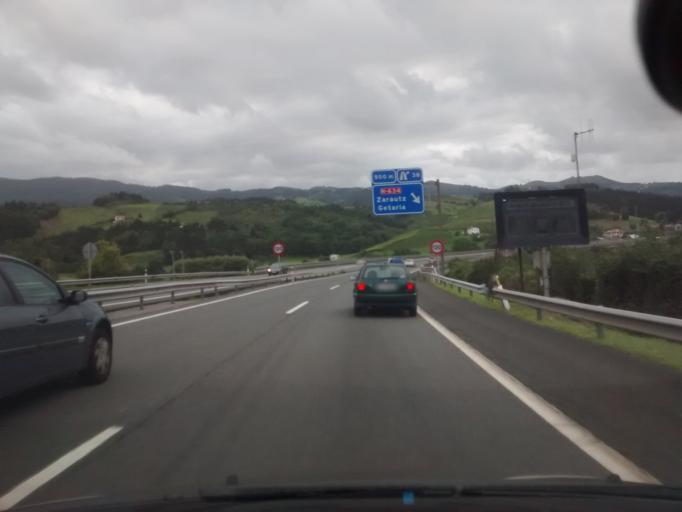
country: ES
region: Basque Country
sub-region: Provincia de Guipuzcoa
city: Orio
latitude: 43.2804
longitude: -2.1470
